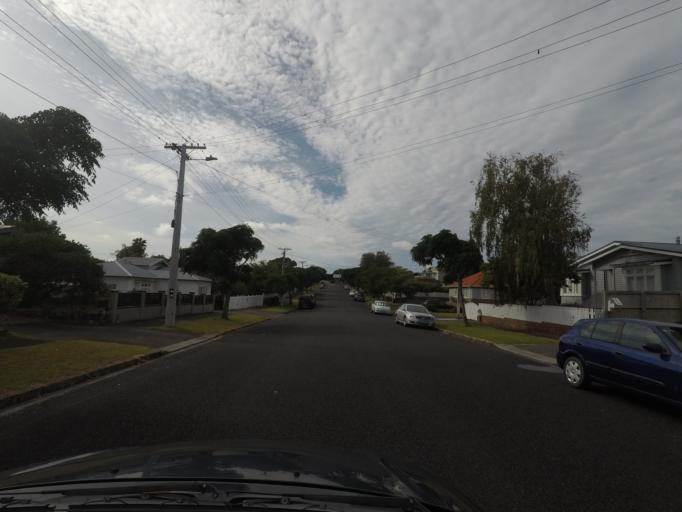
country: NZ
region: Auckland
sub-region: Auckland
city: Rosebank
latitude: -36.8752
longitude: 174.7179
